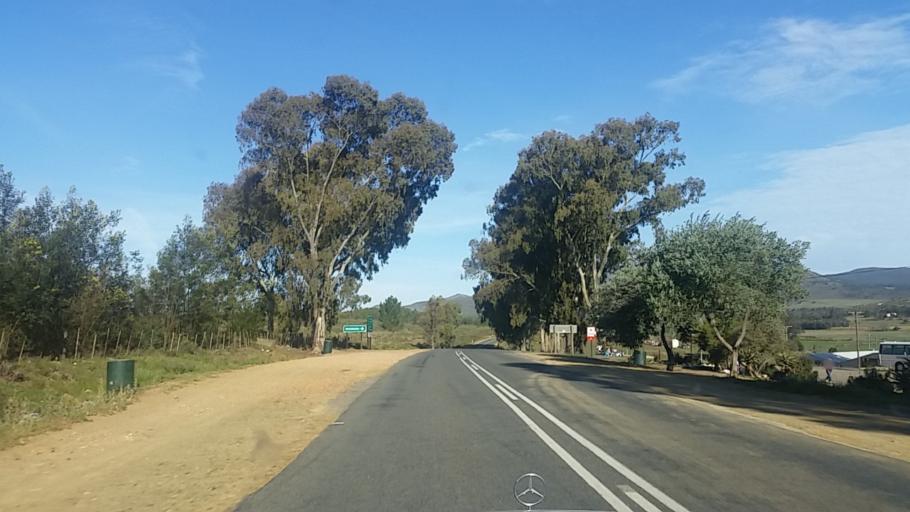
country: ZA
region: Western Cape
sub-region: Eden District Municipality
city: Knysna
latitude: -33.7621
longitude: 22.8830
